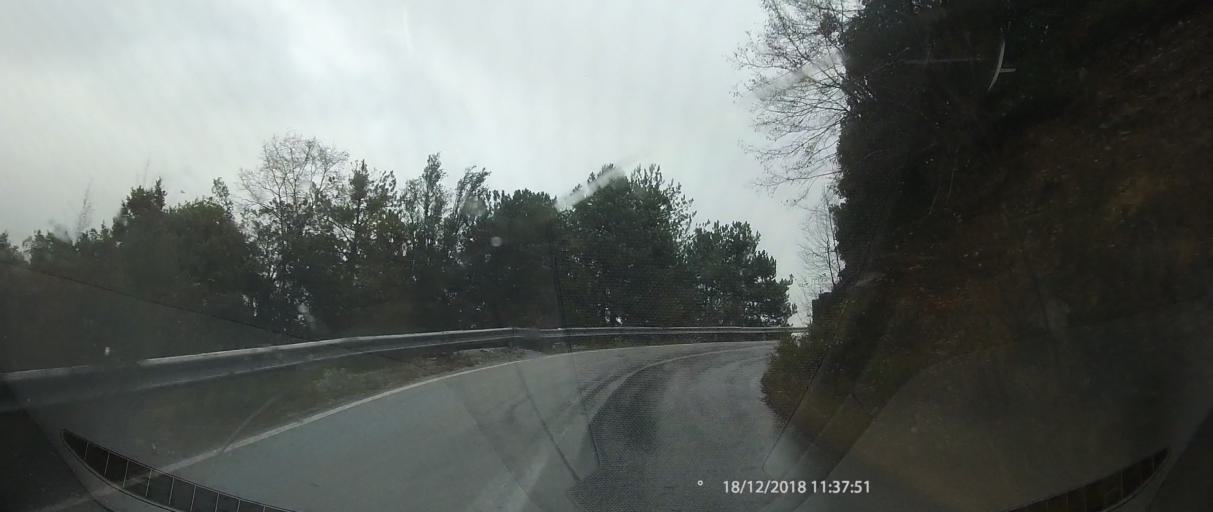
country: GR
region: Central Macedonia
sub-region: Nomos Pierias
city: Litochoro
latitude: 40.1145
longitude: 22.4798
